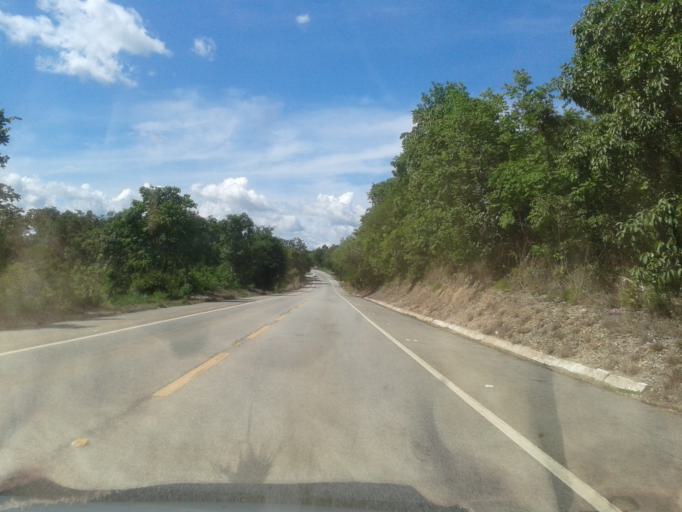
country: BR
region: Goias
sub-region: Goias
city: Goias
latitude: -15.7206
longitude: -50.1878
